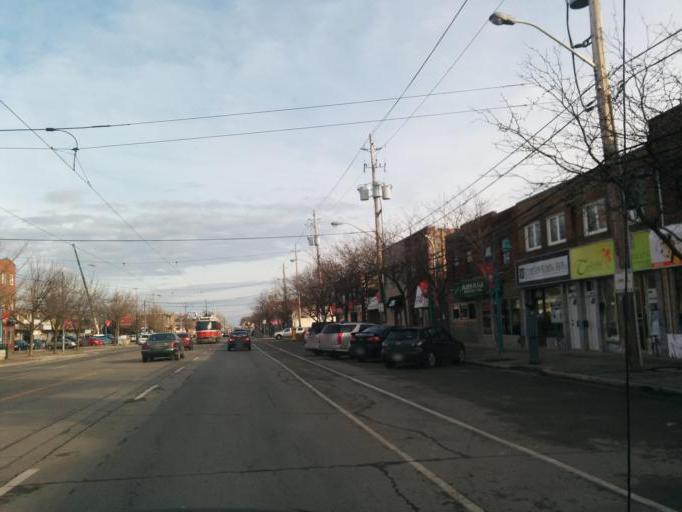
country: CA
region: Ontario
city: Etobicoke
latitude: 43.5964
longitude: -79.5248
